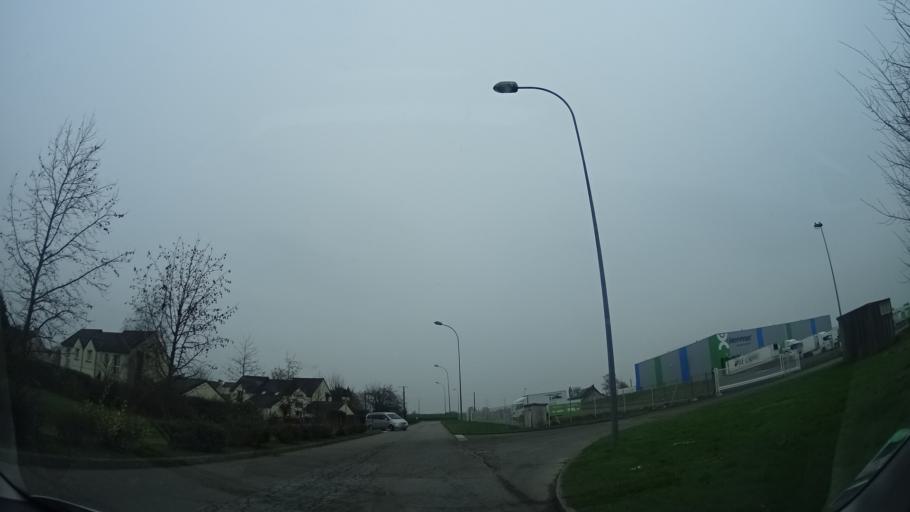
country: FR
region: Brittany
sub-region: Departement d'Ille-et-Vilaine
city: Brece
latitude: 48.1058
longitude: -1.4795
